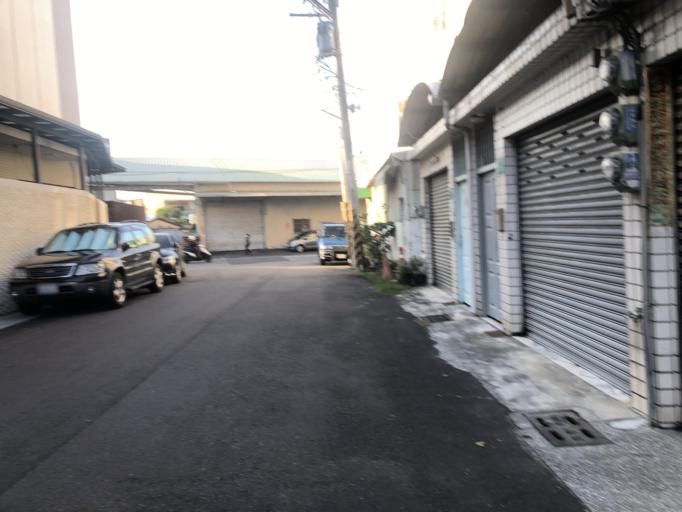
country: TW
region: Taiwan
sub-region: Tainan
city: Tainan
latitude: 23.0379
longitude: 120.1851
